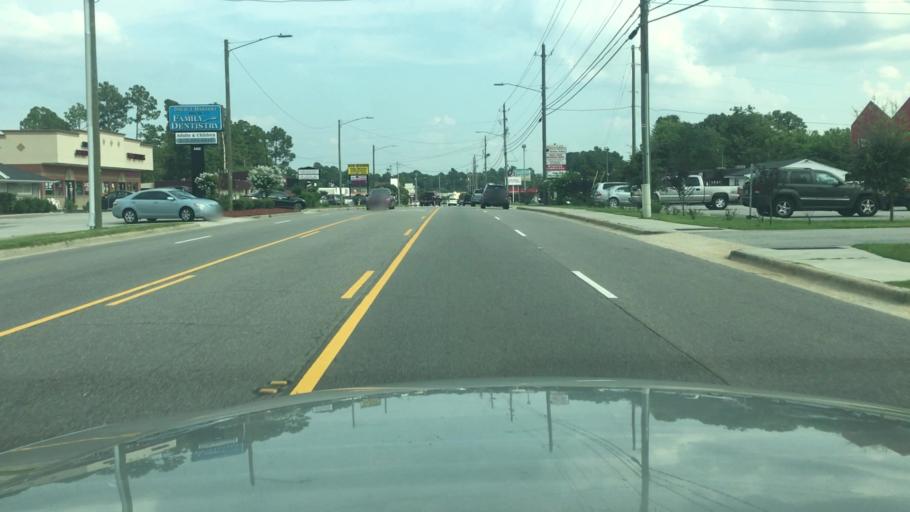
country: US
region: North Carolina
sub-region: Cumberland County
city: Fort Bragg
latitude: 35.1037
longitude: -78.9933
